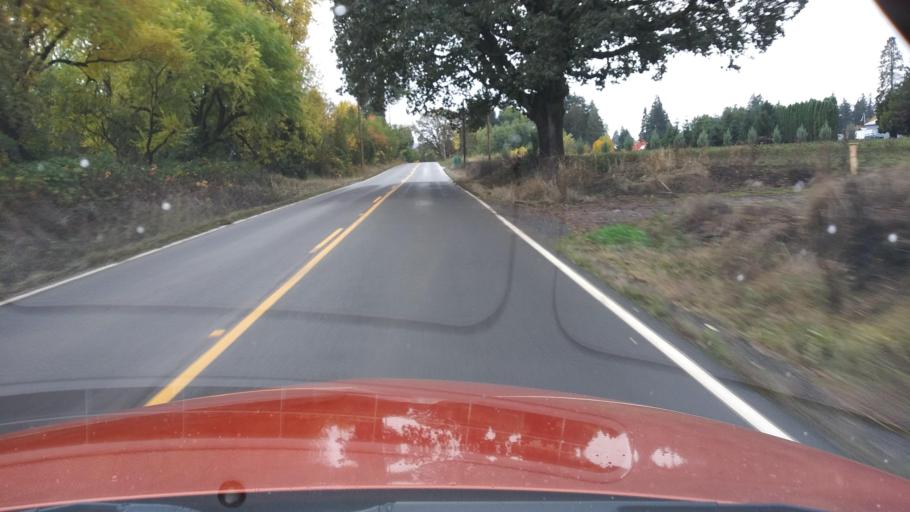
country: US
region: Oregon
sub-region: Washington County
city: Forest Grove
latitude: 45.5330
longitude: -123.0871
